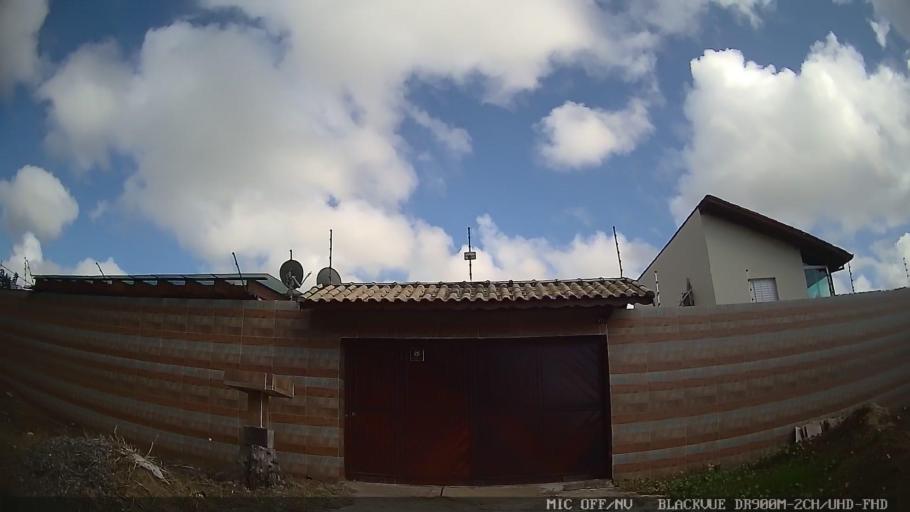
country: BR
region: Sao Paulo
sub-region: Peruibe
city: Peruibe
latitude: -24.2709
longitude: -46.9426
